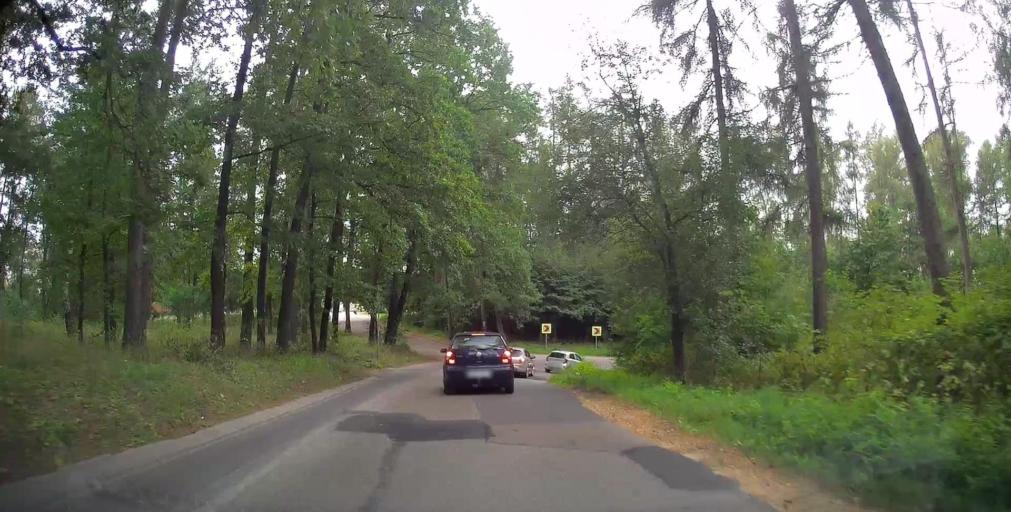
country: PL
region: Lesser Poland Voivodeship
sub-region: Powiat chrzanowski
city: Alwernia
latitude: 50.0733
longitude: 19.5507
